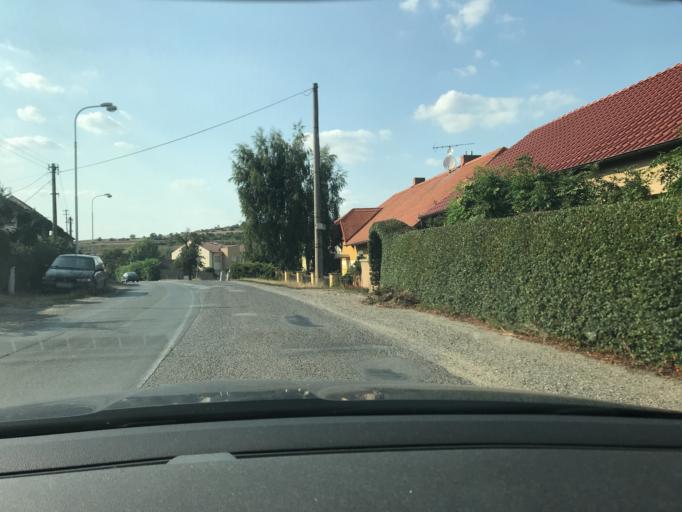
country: CZ
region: Central Bohemia
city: Kralupy nad Vltavou
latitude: 50.2309
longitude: 14.2900
